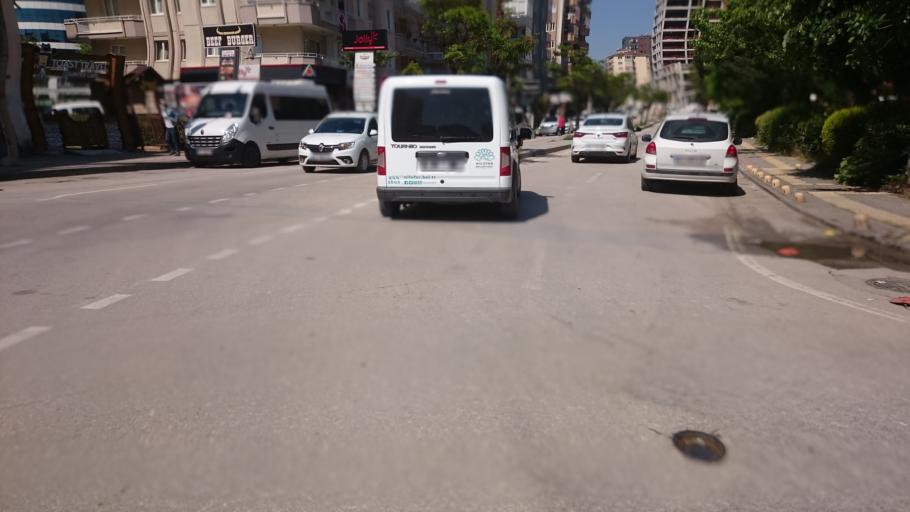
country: TR
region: Bursa
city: Yildirim
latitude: 40.2131
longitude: 28.9810
